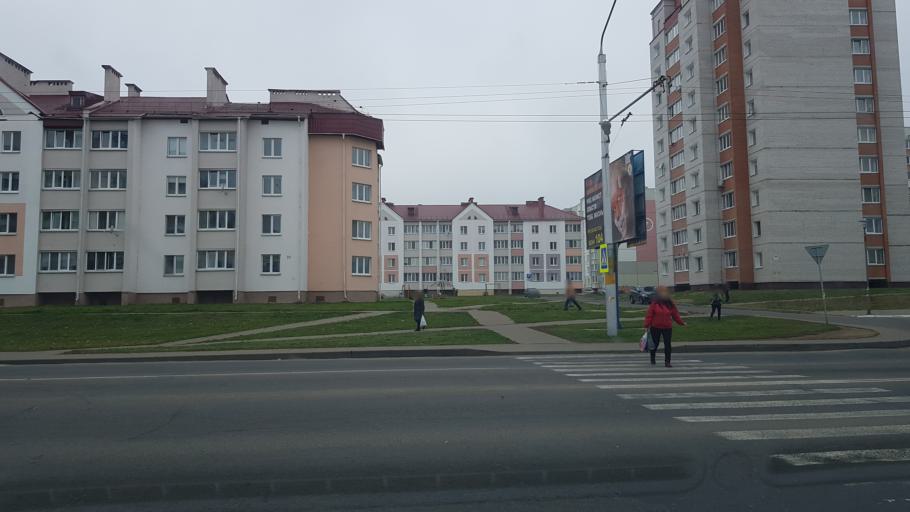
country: BY
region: Mogilev
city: Babruysk
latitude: 53.1877
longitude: 29.2255
